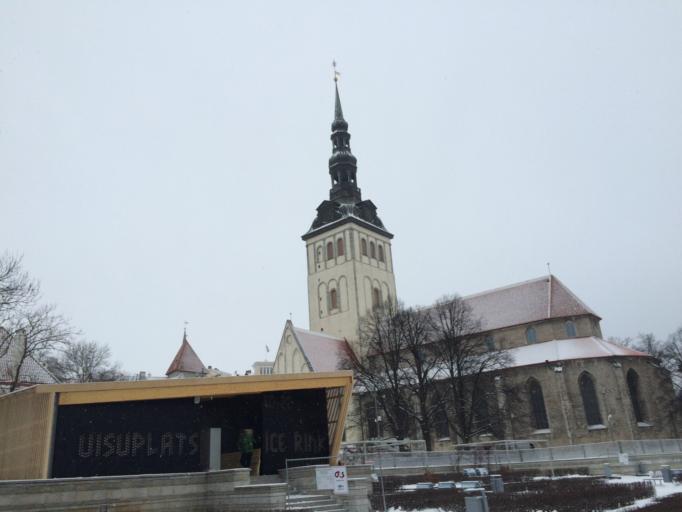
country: EE
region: Harju
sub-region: Tallinna linn
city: Tallinn
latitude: 59.4350
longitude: 24.7436
